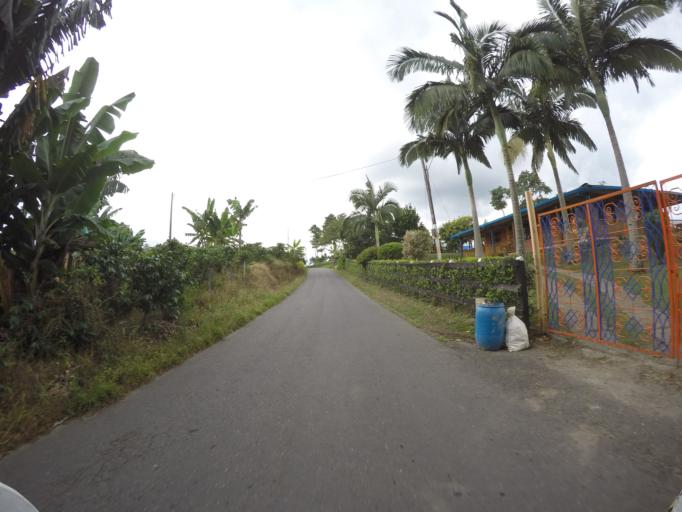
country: CO
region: Quindio
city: Quimbaya
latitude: 4.6116
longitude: -75.7135
